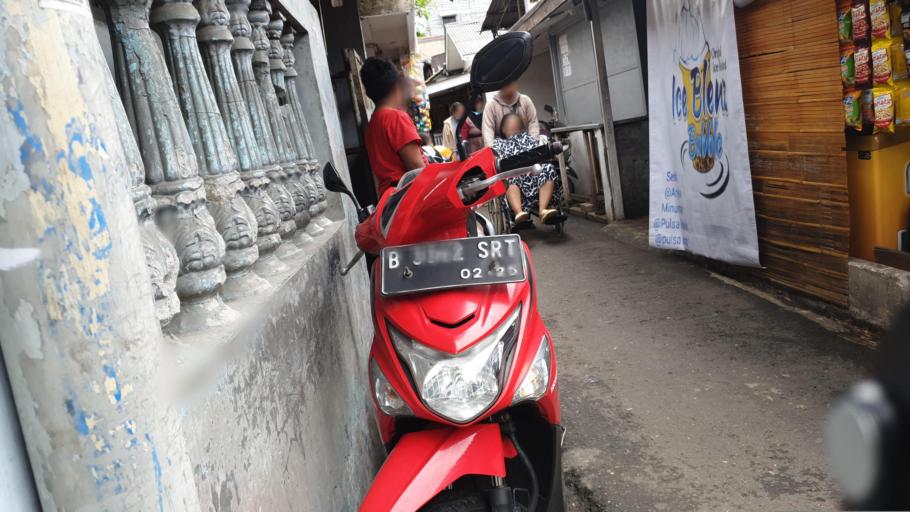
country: ID
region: Jakarta Raya
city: Jakarta
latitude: -6.2461
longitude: 106.7831
